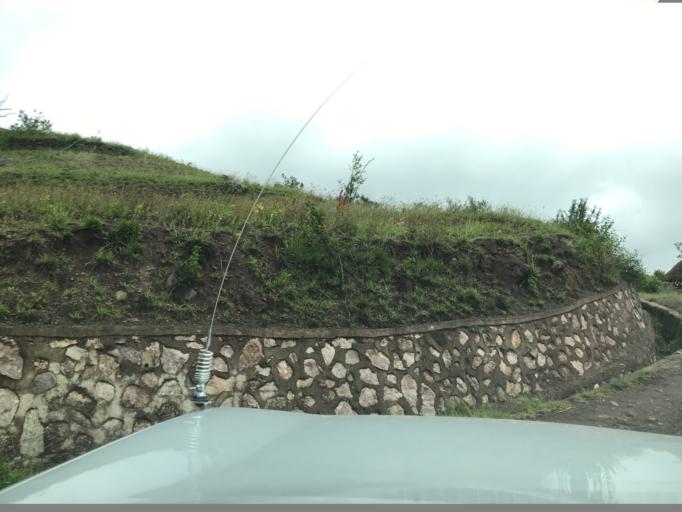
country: TL
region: Aileu
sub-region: Aileu Villa
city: Aileu
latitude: -8.8637
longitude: 125.5593
